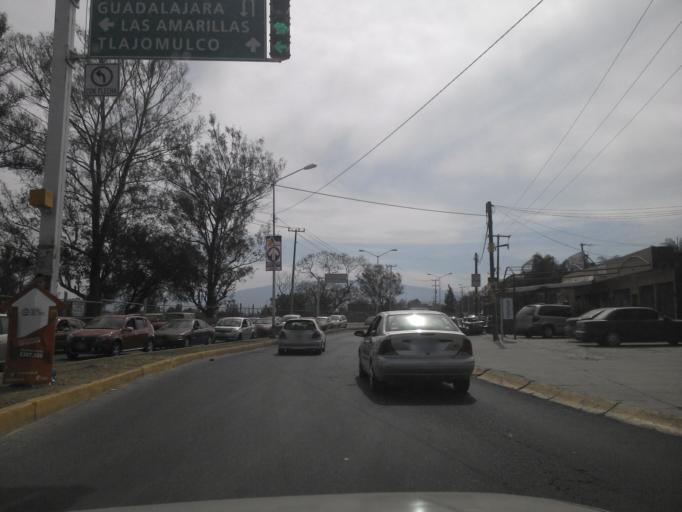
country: MX
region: Jalisco
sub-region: San Pedro Tlaquepaque
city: Paseo del Prado
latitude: 20.5630
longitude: -103.3923
